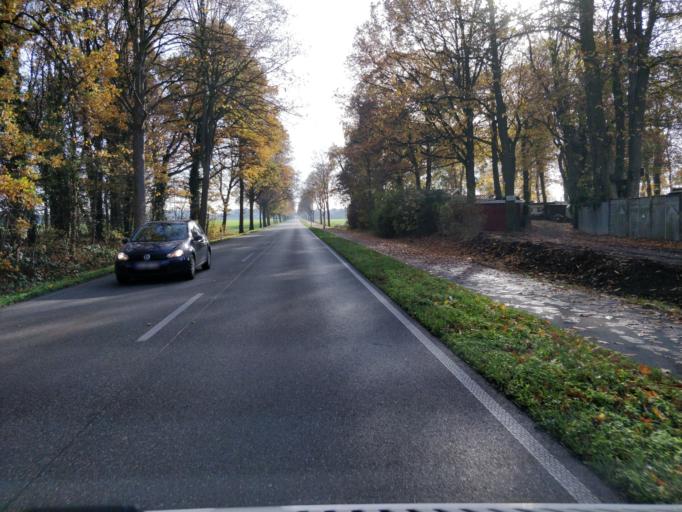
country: DE
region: North Rhine-Westphalia
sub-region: Regierungsbezirk Dusseldorf
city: Mehrhoog
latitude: 51.7461
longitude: 6.4916
